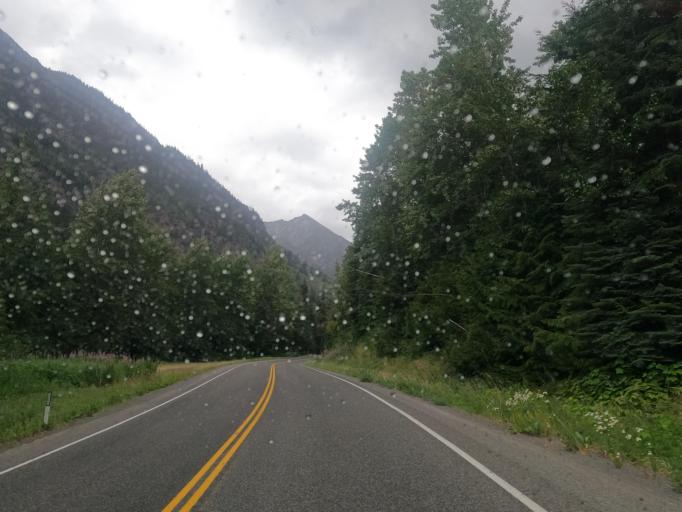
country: CA
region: British Columbia
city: Lillooet
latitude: 50.4794
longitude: -122.2156
